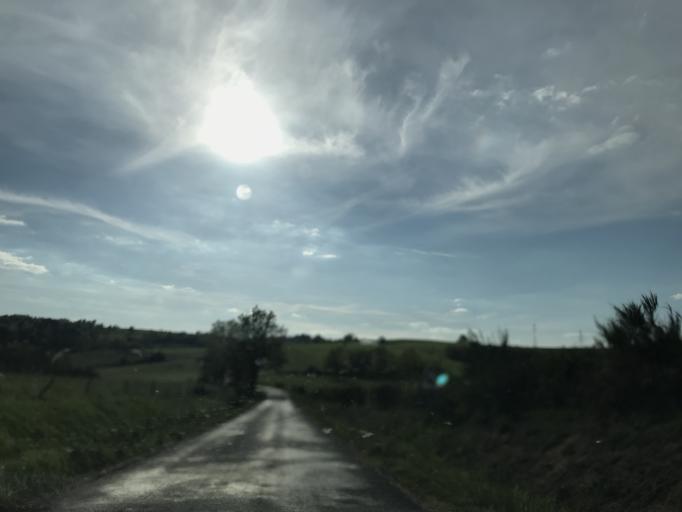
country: FR
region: Auvergne
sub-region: Departement du Puy-de-Dome
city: Courpiere
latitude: 45.7392
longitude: 3.5069
